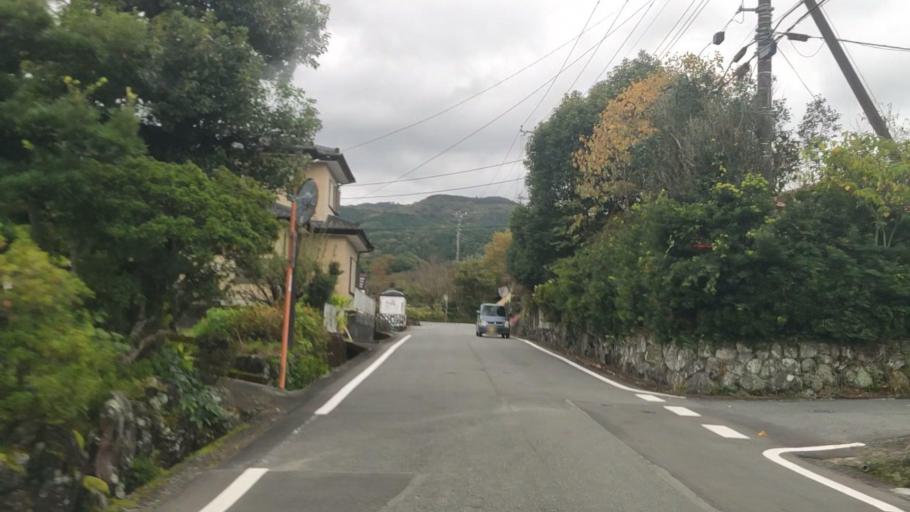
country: JP
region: Shizuoka
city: Ito
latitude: 34.9169
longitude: 138.9923
